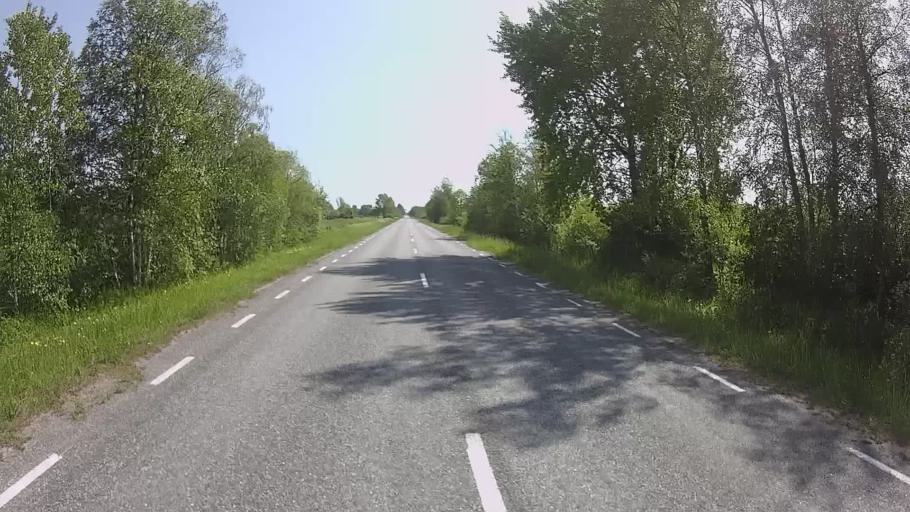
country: EE
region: Saare
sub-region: Kuressaare linn
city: Kuressaare
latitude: 58.3718
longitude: 22.0446
